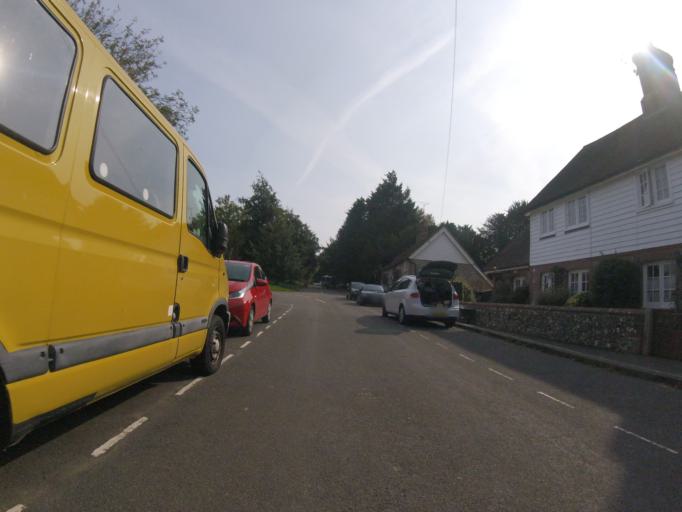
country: GB
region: England
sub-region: Brighton and Hove
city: Rottingdean
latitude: 50.8626
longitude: -0.0783
